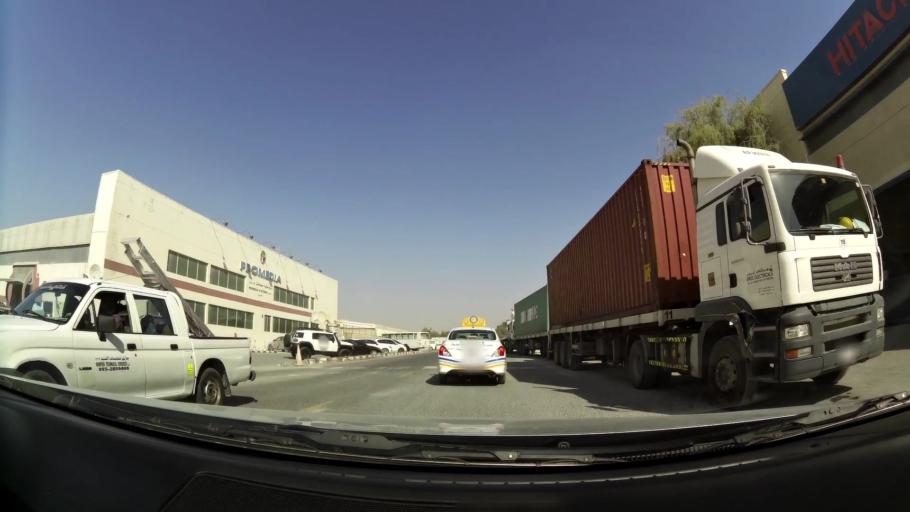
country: AE
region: Dubai
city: Dubai
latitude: 25.1271
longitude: 55.2185
